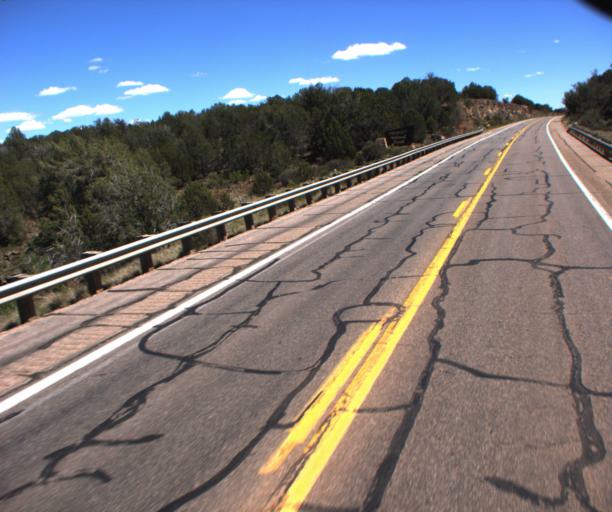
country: US
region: Arizona
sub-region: Yavapai County
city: Paulden
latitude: 35.0810
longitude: -112.4051
